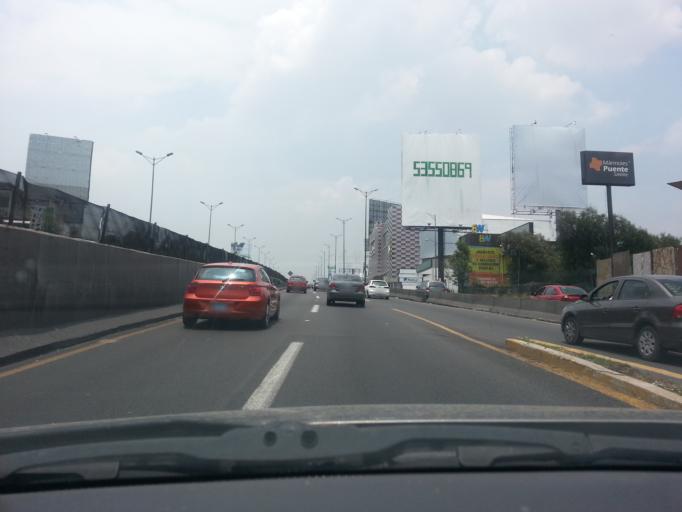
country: MX
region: Mexico
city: Naucalpan de Juarez
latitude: 19.5013
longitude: -99.2368
